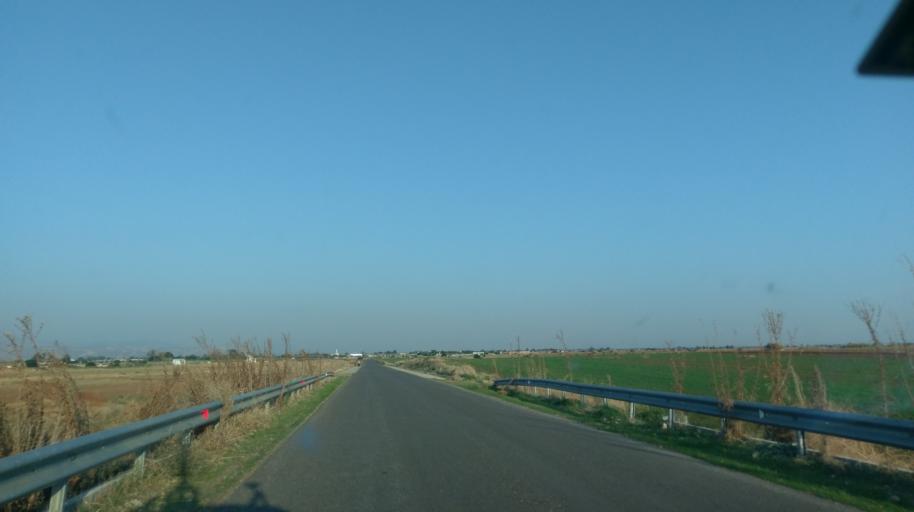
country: CY
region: Lefkosia
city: Morfou
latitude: 35.1521
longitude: 32.9860
